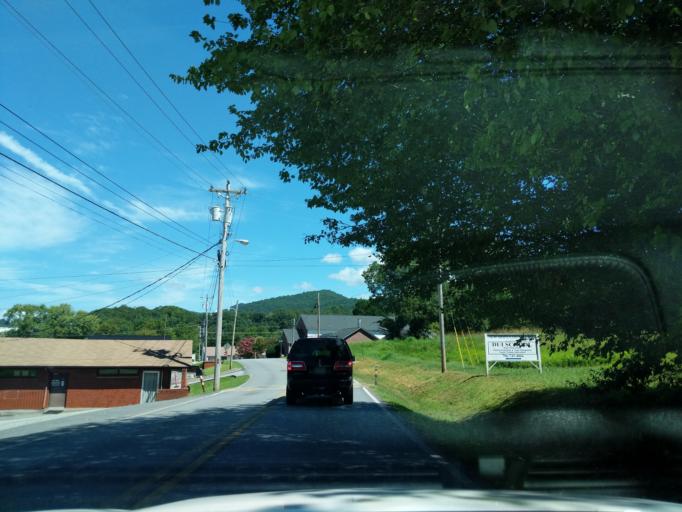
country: US
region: Georgia
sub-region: Union County
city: Blairsville
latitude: 34.8725
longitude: -83.9588
